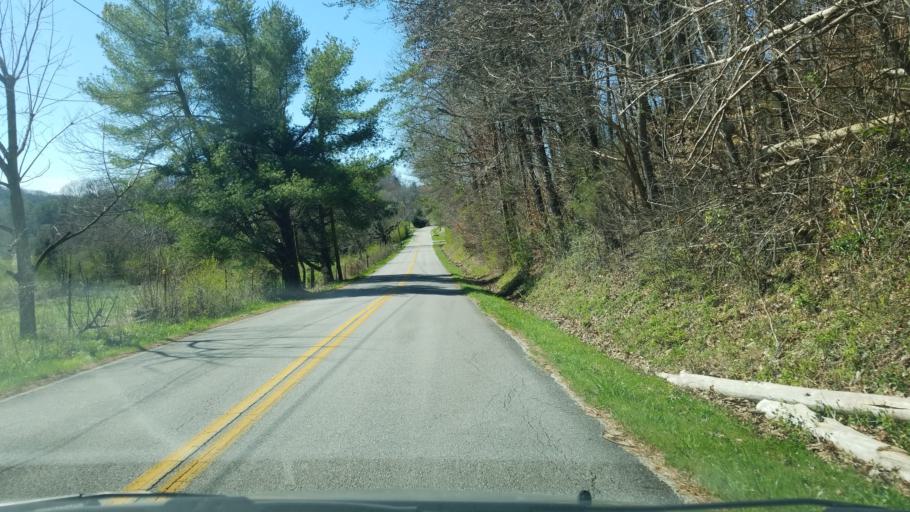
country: US
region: Tennessee
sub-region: Hamilton County
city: Falling Water
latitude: 35.1807
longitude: -85.2551
